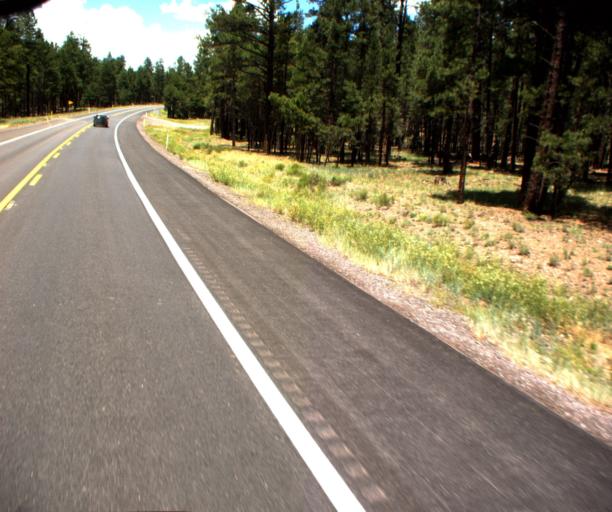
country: US
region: Arizona
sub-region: Coconino County
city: Flagstaff
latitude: 35.2547
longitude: -111.7011
